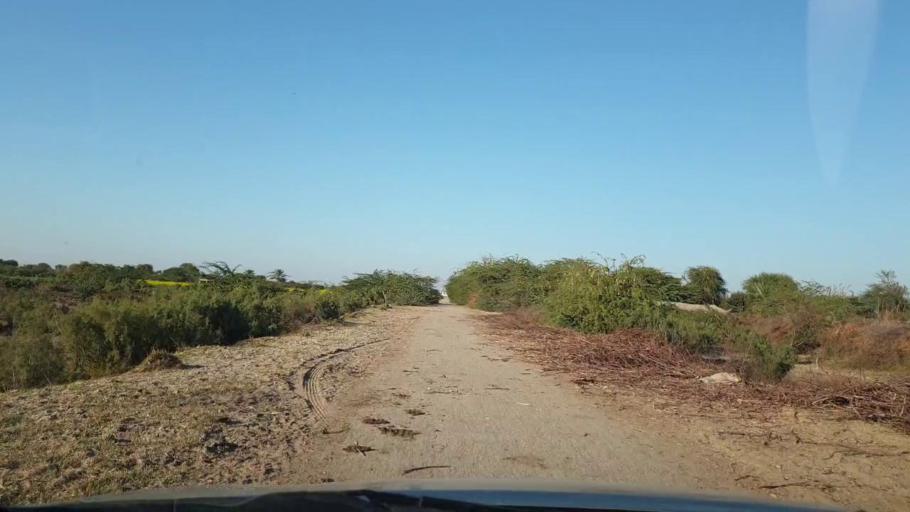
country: PK
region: Sindh
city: Jhol
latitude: 25.9018
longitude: 68.9250
